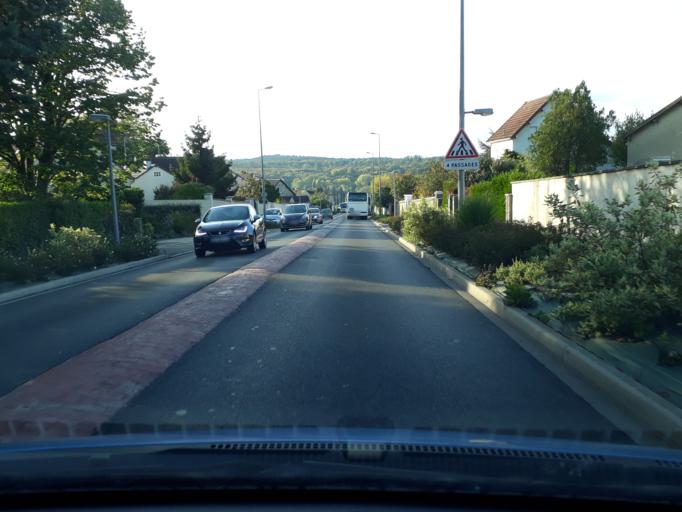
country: FR
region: Ile-de-France
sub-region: Departement de Seine-et-Marne
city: Samoreau
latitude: 48.4256
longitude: 2.7601
